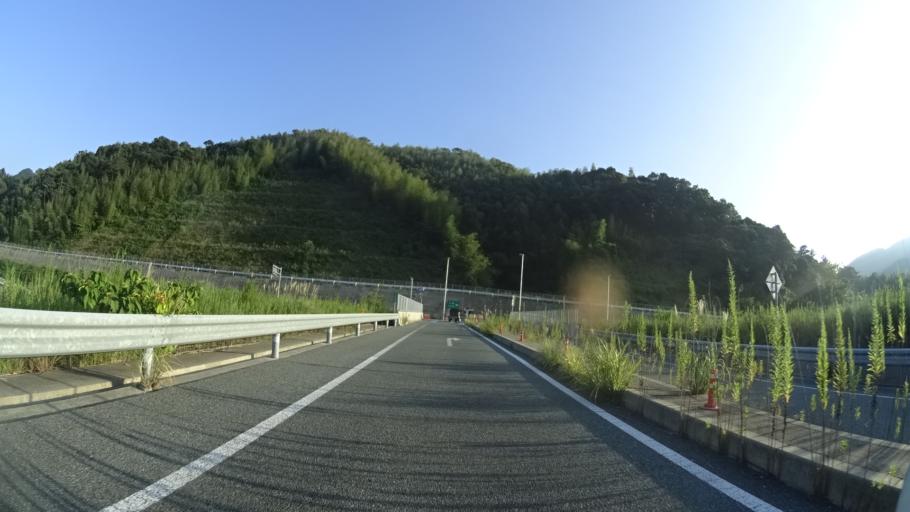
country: JP
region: Yamaguchi
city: Hagi
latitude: 34.3862
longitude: 131.3497
